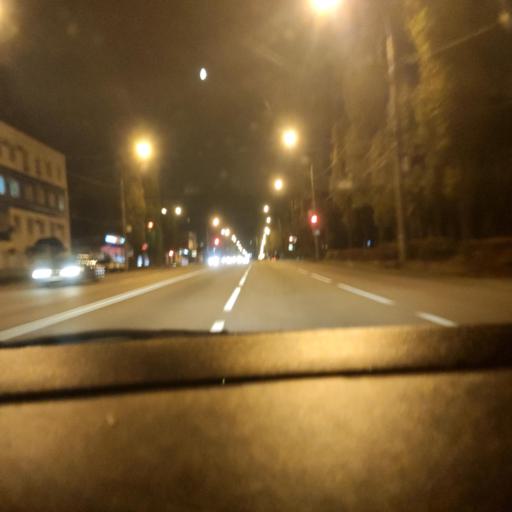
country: RU
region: Voronezj
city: Voronezh
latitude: 51.6887
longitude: 39.1651
